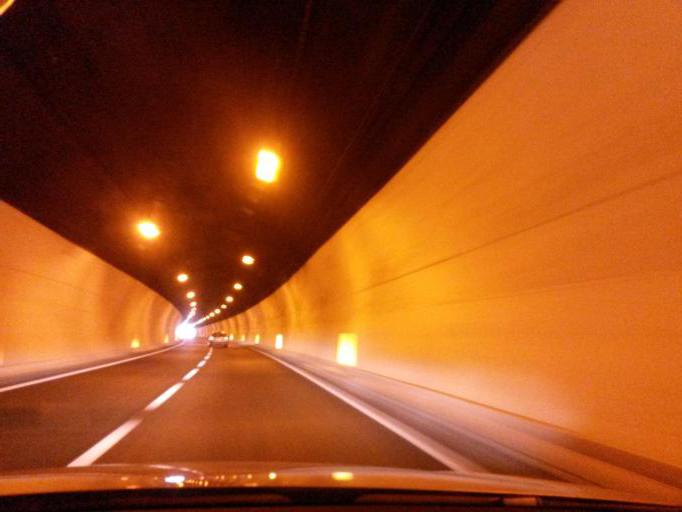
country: IT
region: Liguria
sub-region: Provincia di La Spezia
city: Framura
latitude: 44.2424
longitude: 9.5487
